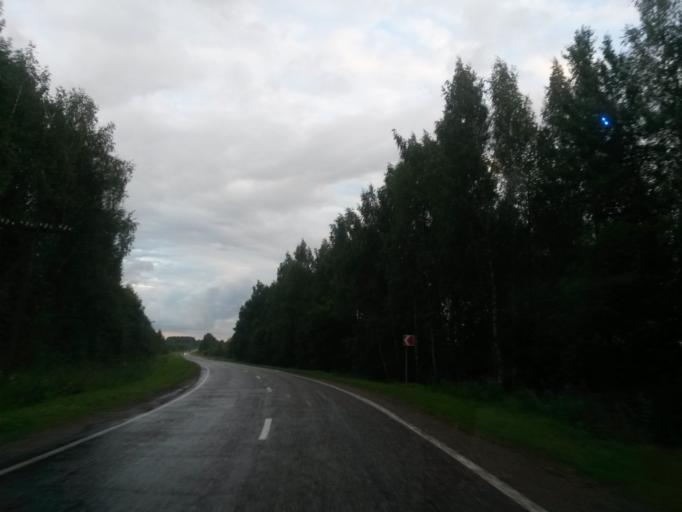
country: RU
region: Jaroslavl
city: Tutayev
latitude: 57.9139
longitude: 39.5156
